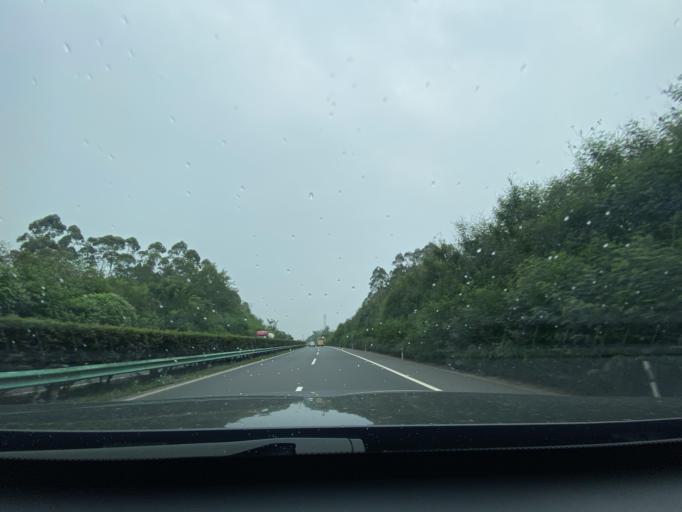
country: CN
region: Sichuan
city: Longquan
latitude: 30.3213
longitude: 104.1209
